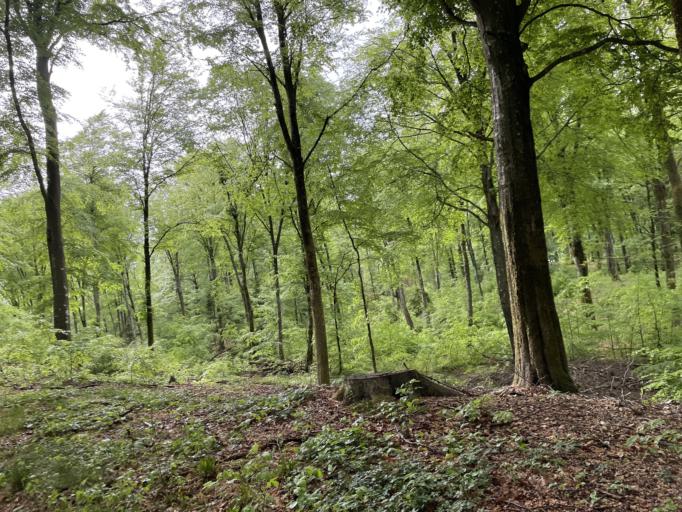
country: SE
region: Skane
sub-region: Hassleholms Kommun
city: Sosdala
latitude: 56.0601
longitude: 13.6730
